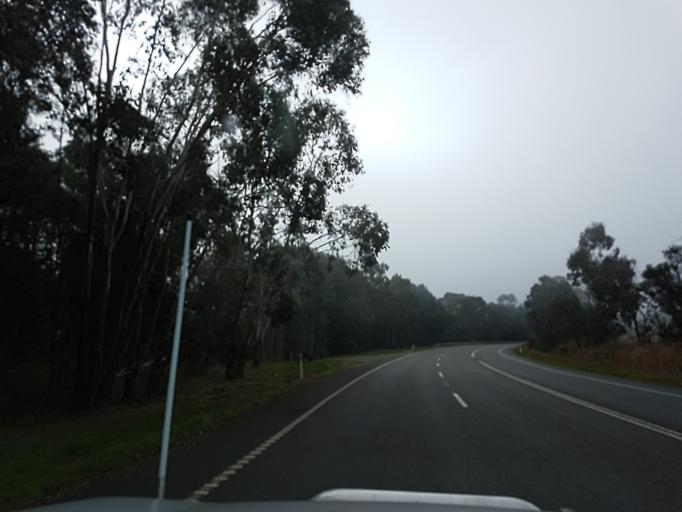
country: AU
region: Victoria
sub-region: Murrindindi
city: Kinglake West
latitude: -37.3164
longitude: 145.4506
